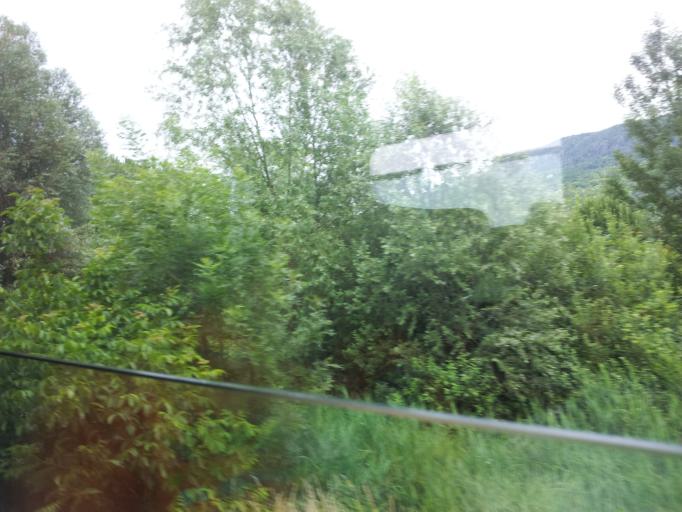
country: HU
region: Veszprem
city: Badacsonytomaj
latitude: 46.7957
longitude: 17.4701
